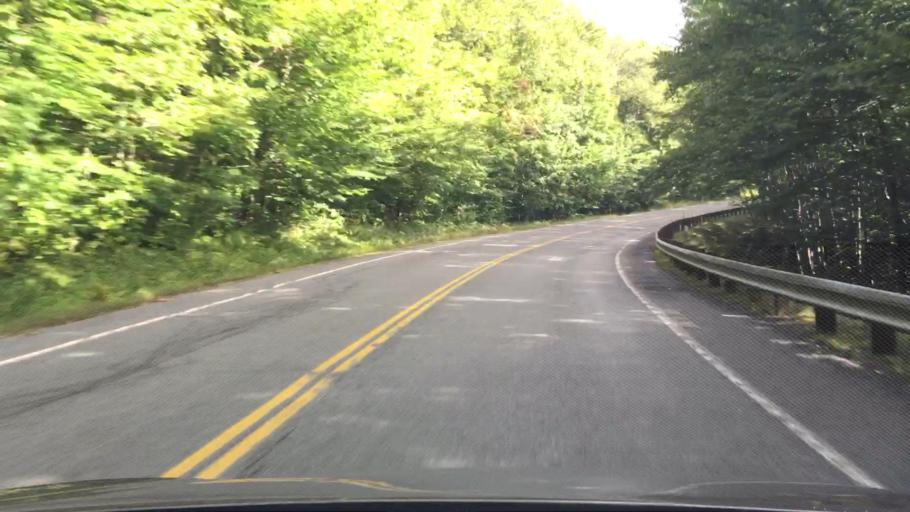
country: US
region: New Hampshire
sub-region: Grafton County
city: Woodstock
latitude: 44.0576
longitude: -71.5840
